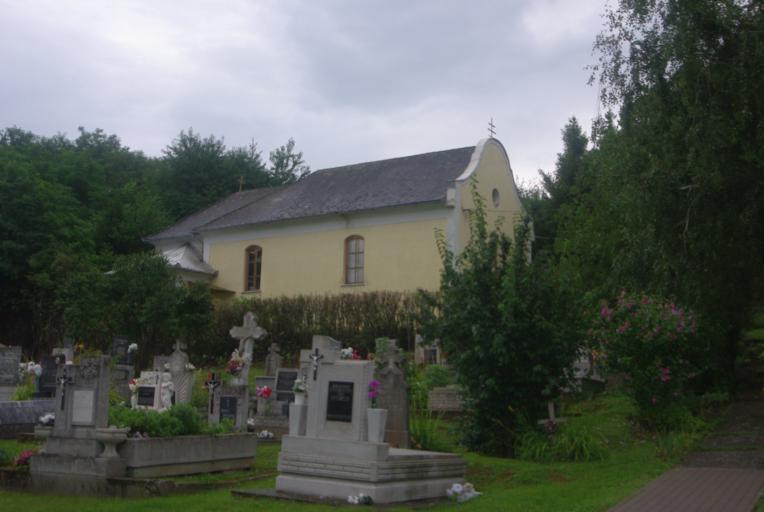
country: HU
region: Borsod-Abauj-Zemplen
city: Gonc
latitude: 48.3935
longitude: 21.3462
